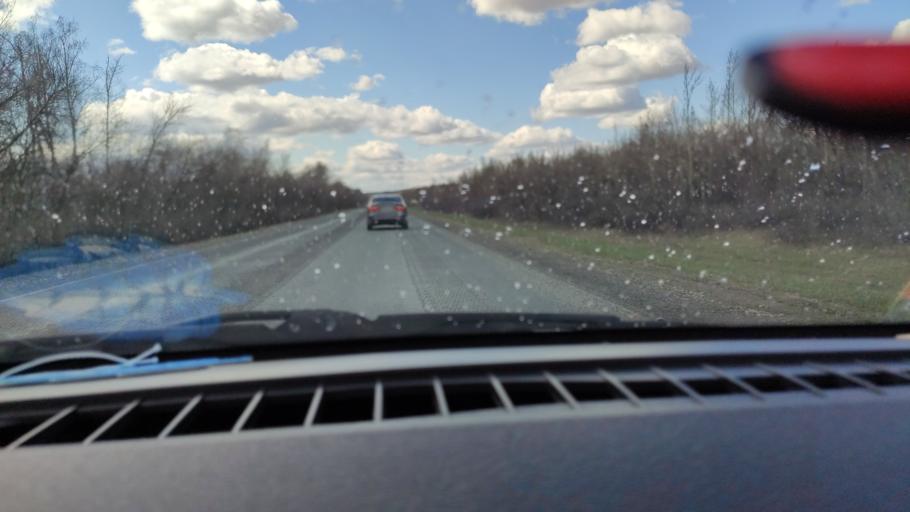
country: RU
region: Saratov
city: Dukhovnitskoye
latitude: 52.6634
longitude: 48.2136
